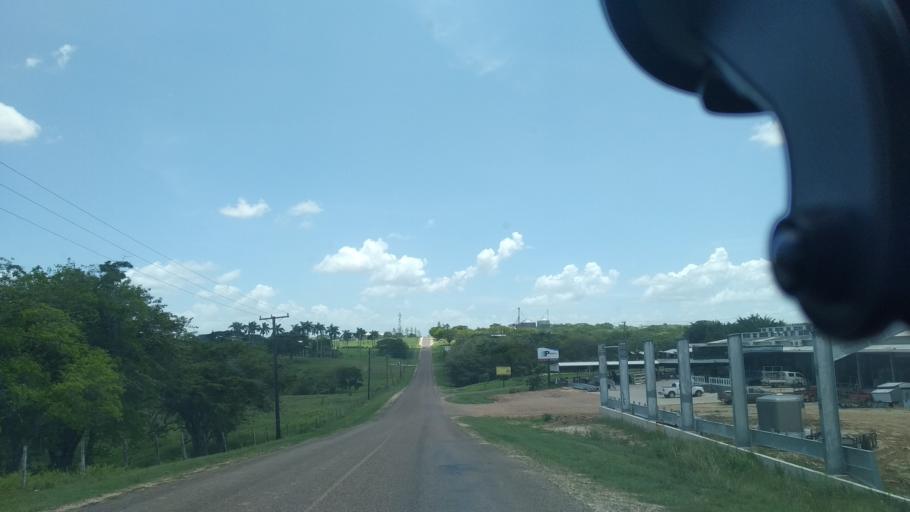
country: BZ
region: Cayo
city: San Ignacio
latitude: 17.2566
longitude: -88.9919
